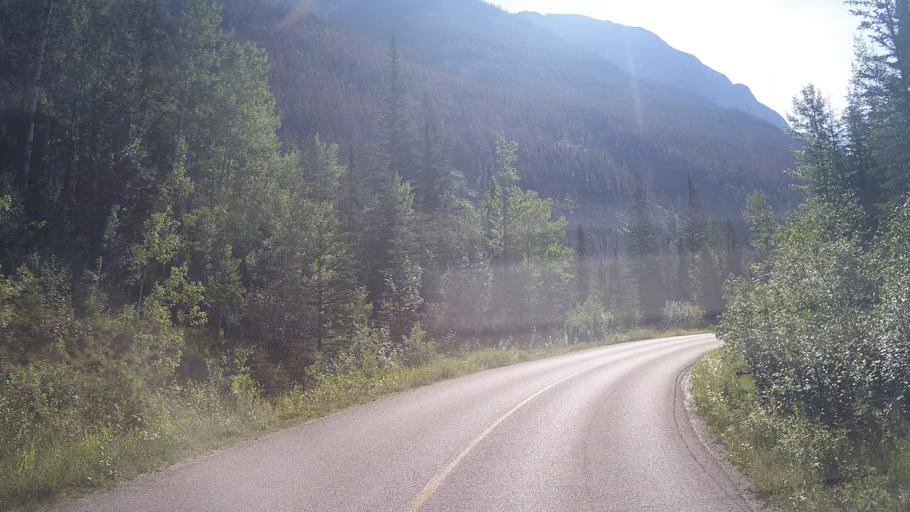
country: CA
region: Alberta
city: Hinton
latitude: 53.1783
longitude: -117.8351
